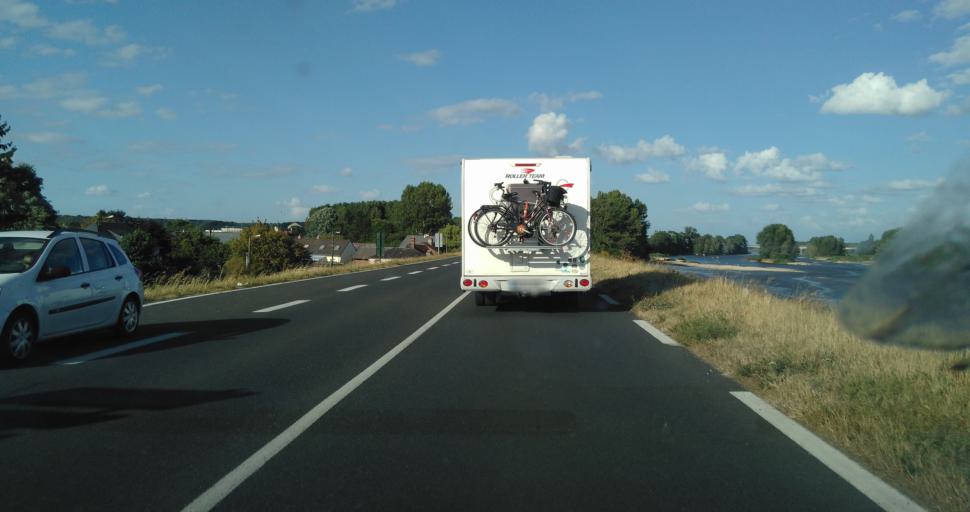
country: FR
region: Centre
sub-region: Departement d'Indre-et-Loire
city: Amboise
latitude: 47.4205
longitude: 0.9857
